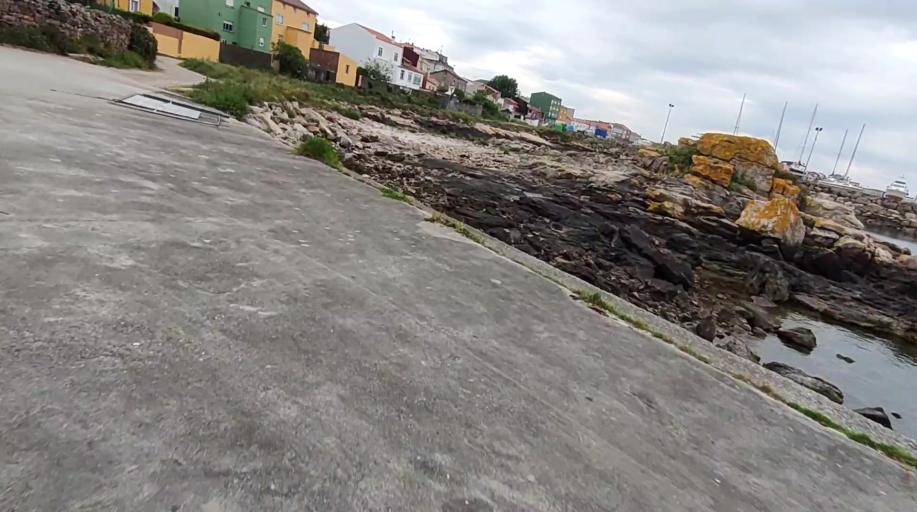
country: ES
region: Galicia
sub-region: Provincia da Coruna
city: Boiro
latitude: 42.6197
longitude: -8.8876
